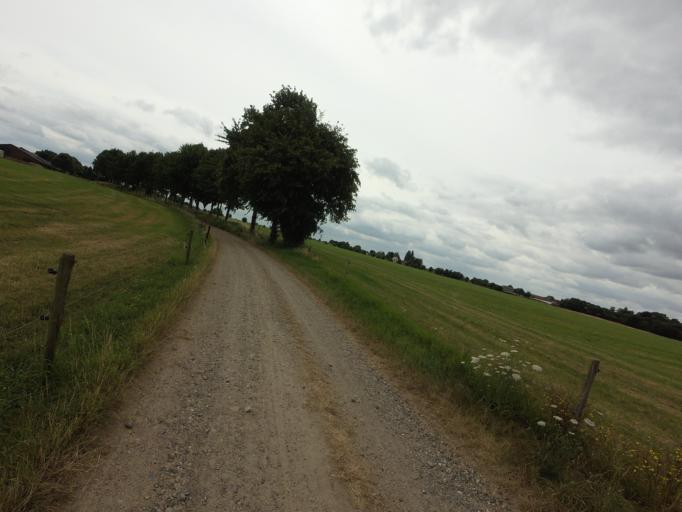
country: NL
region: Limburg
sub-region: Valkenburg aan de Geul
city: Berg
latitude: 50.8459
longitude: 5.7956
